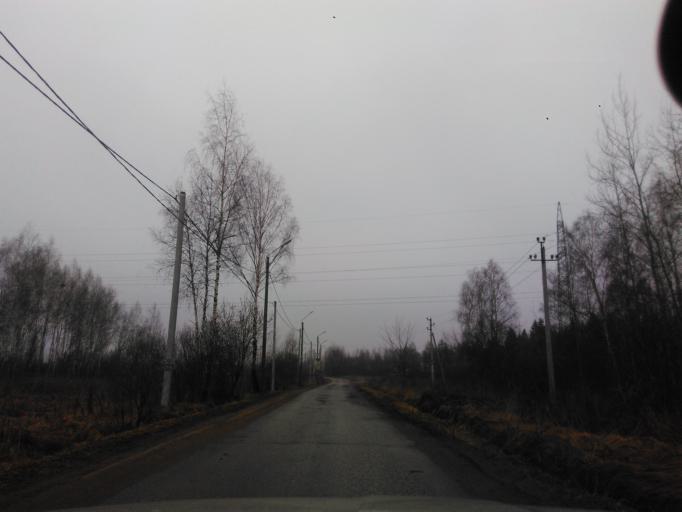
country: RU
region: Moskovskaya
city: Andreyevka
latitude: 55.9270
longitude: 37.1500
